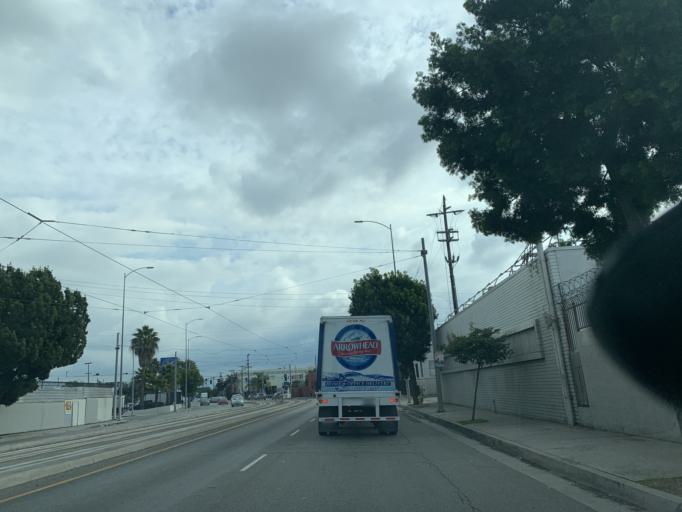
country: US
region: California
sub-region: Los Angeles County
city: Los Angeles
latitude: 34.0212
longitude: -118.2449
